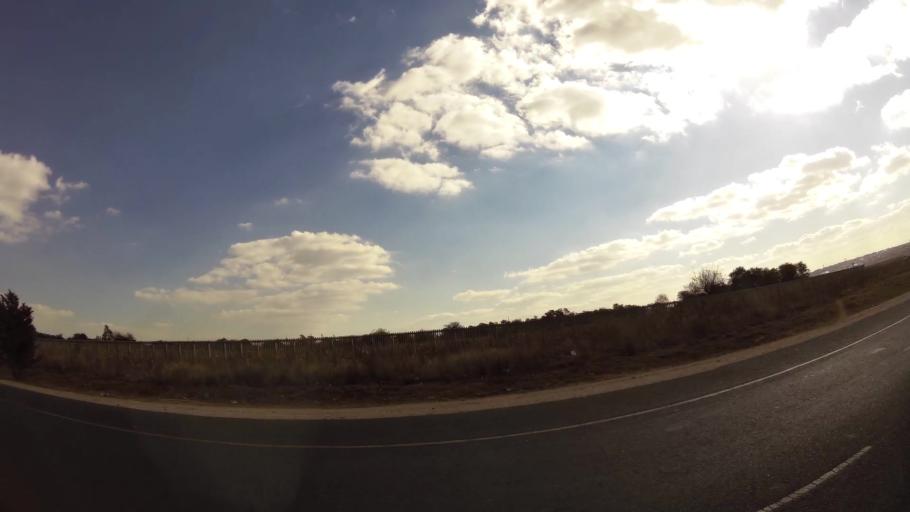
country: ZA
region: Gauteng
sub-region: Ekurhuleni Metropolitan Municipality
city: Tembisa
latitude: -25.9578
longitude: 28.1958
